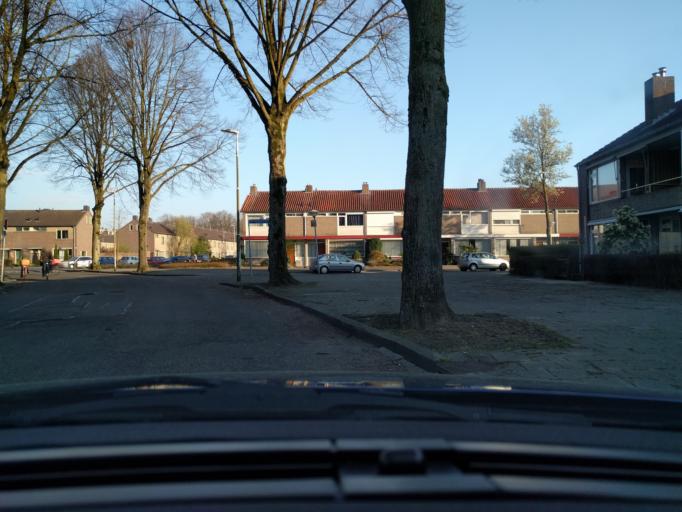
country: NL
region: North Brabant
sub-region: Gemeente Eindhoven
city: Eindhoven
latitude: 51.4634
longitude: 5.4663
